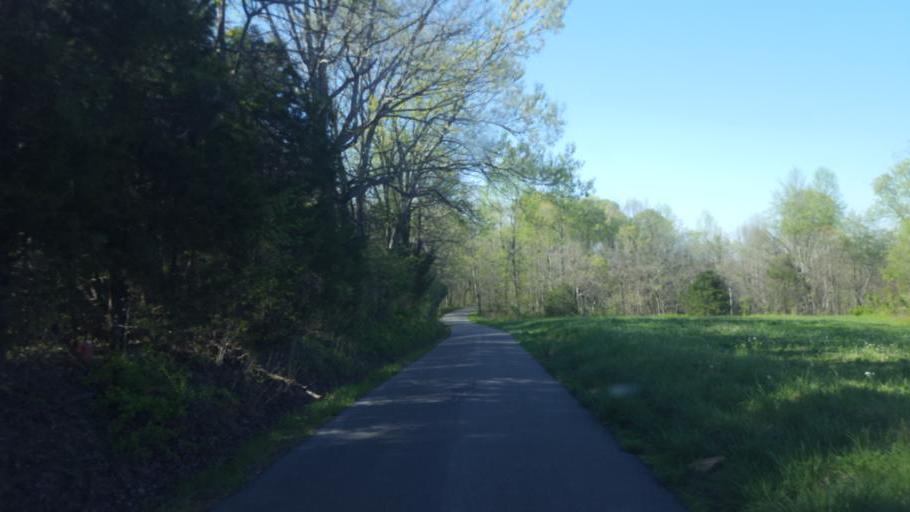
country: US
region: Kentucky
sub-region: Barren County
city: Cave City
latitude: 37.1728
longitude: -86.0431
